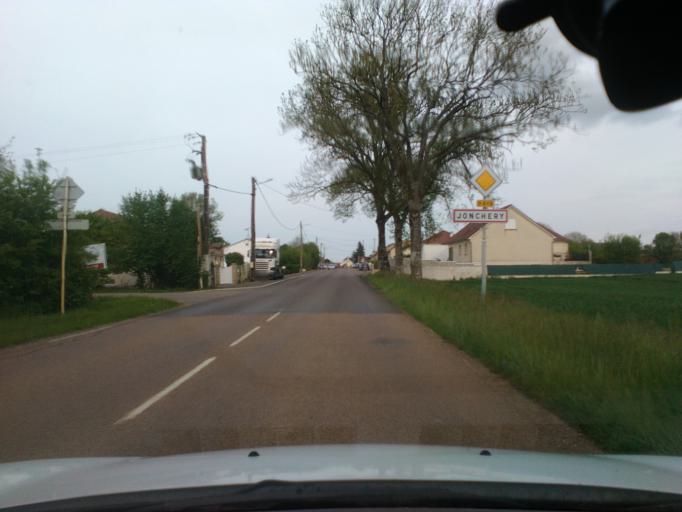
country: FR
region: Champagne-Ardenne
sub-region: Departement de la Haute-Marne
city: Chaumont
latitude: 48.1363
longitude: 5.0802
